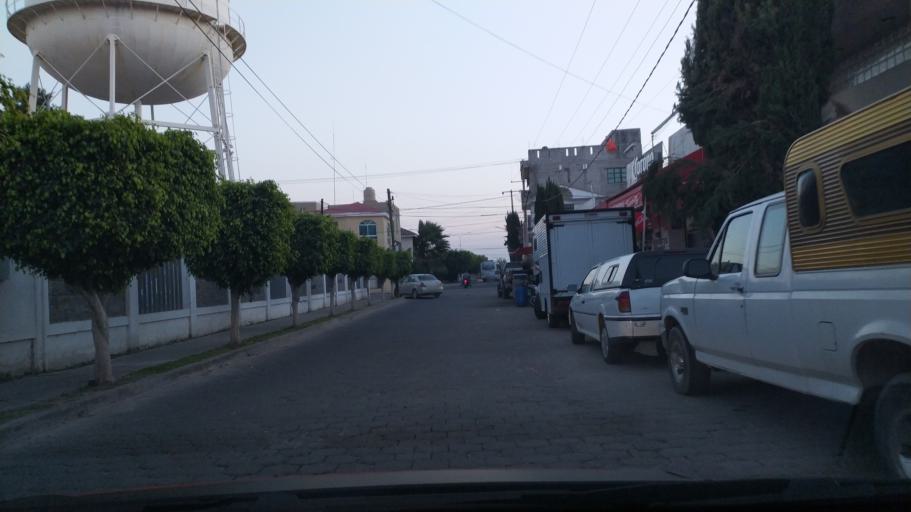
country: MX
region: Guanajuato
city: San Francisco del Rincon
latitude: 21.0090
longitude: -101.8603
